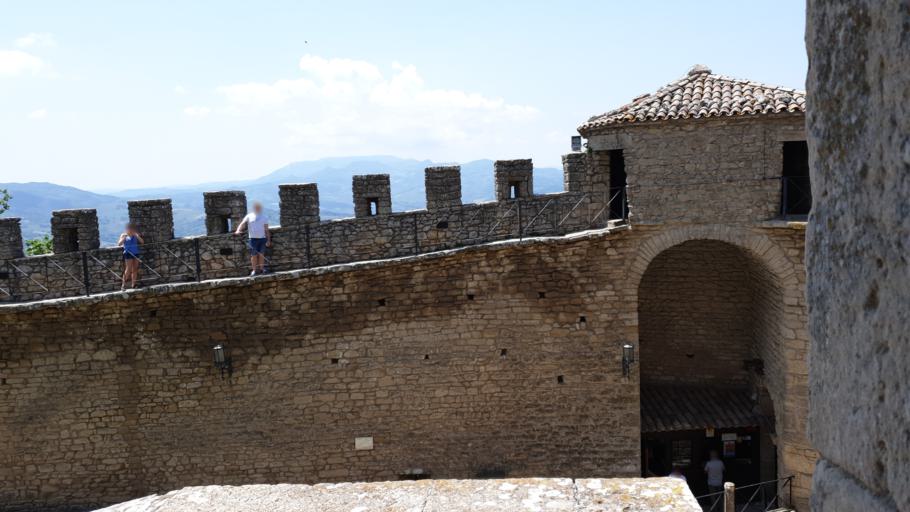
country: SM
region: San Marino
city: San Marino
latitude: 43.9353
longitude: 12.4495
